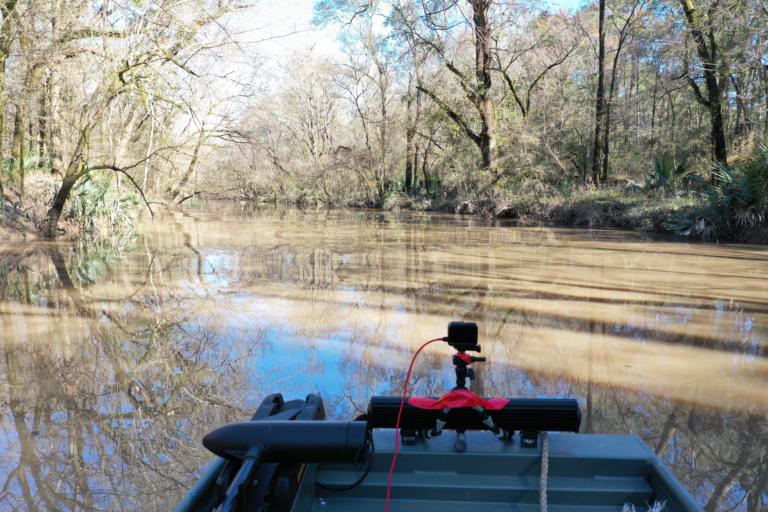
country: US
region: Louisiana
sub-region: Calcasieu Parish
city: Iowa
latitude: 30.3145
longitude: -93.0548
